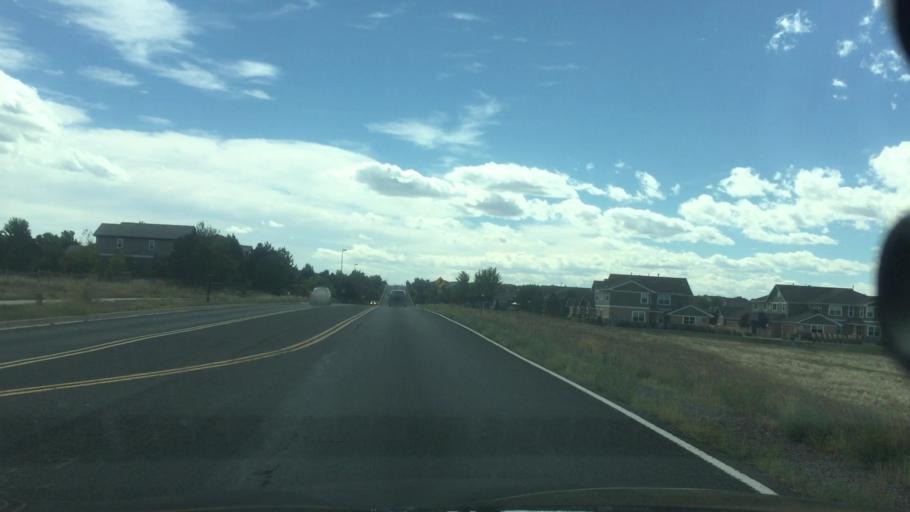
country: US
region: Colorado
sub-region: Arapahoe County
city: Dove Valley
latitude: 39.6511
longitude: -104.7350
